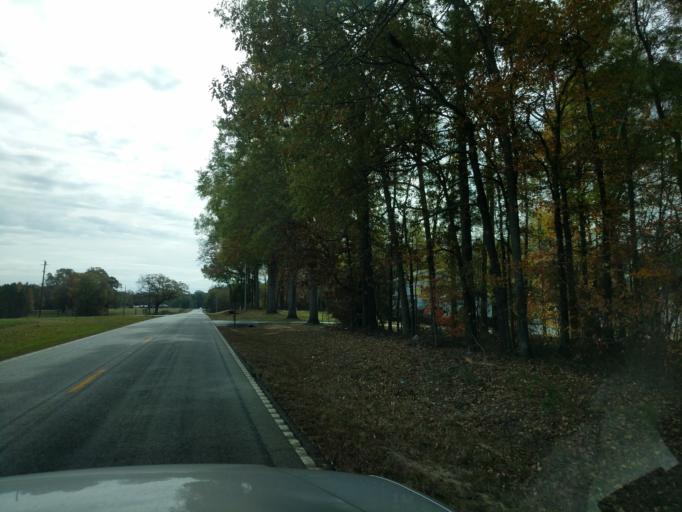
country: US
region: South Carolina
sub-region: Laurens County
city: Joanna
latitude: 34.3563
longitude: -81.8596
